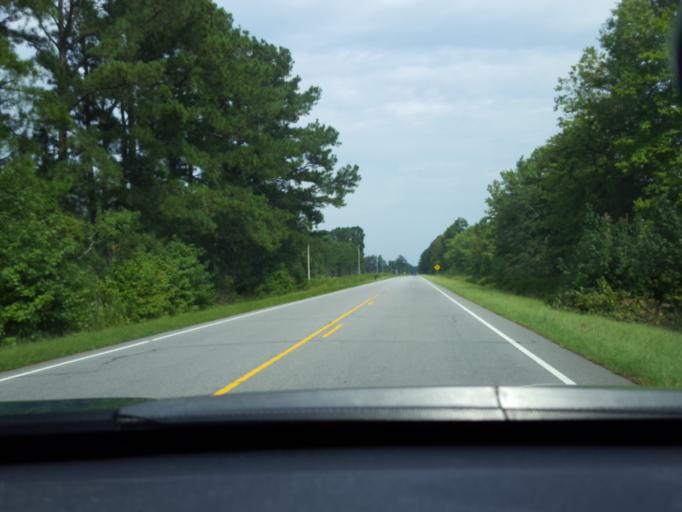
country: US
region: North Carolina
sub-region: Washington County
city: Plymouth
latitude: 35.9756
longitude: -76.7613
